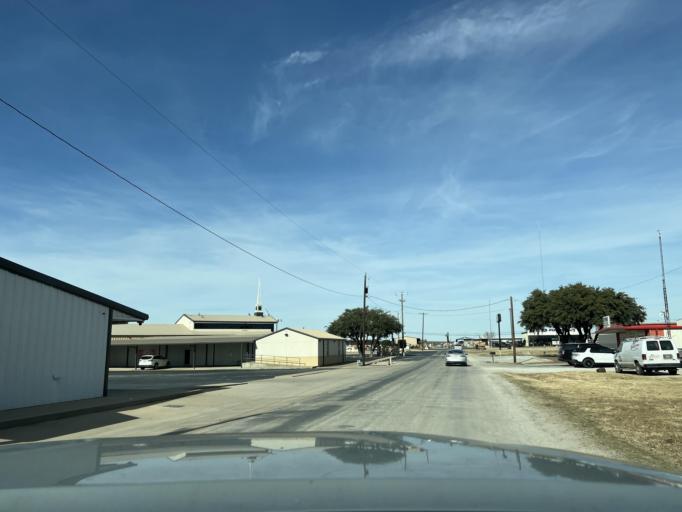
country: US
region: Texas
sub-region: Eastland County
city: Eastland
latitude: 32.4002
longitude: -98.7978
